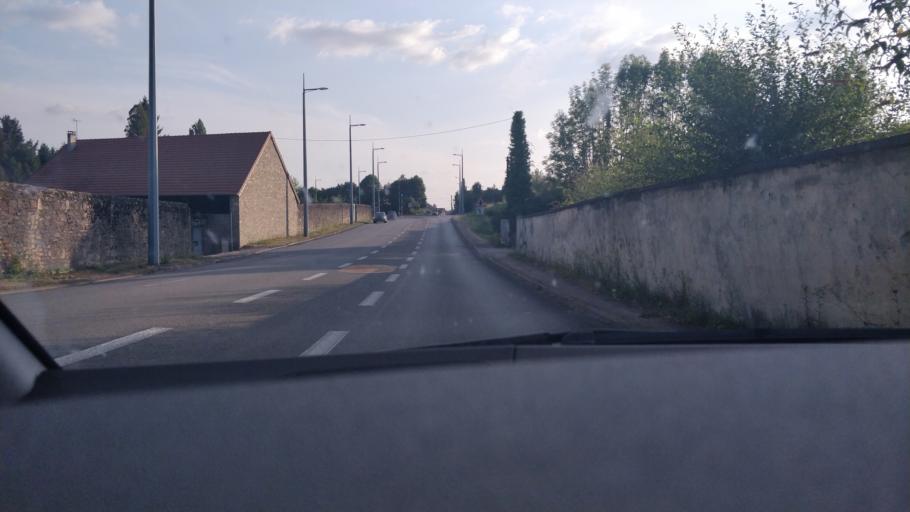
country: FR
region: Limousin
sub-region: Departement de la Haute-Vienne
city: Limoges
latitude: 45.8439
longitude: 1.2891
